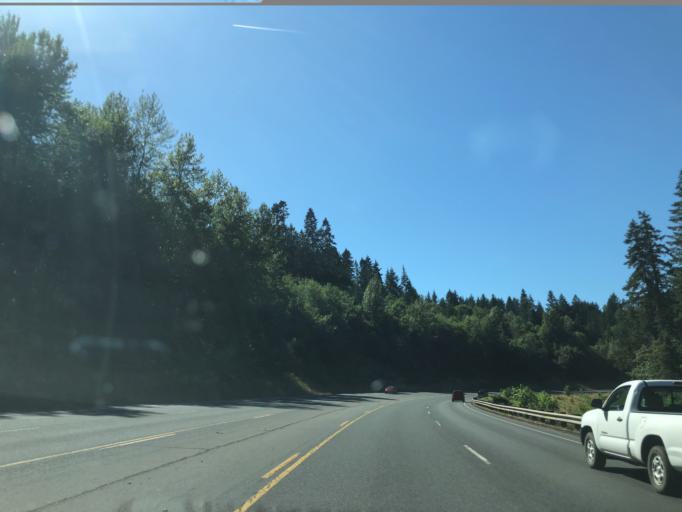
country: US
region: Oregon
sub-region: Linn County
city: Sweet Home
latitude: 44.4051
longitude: -122.7605
